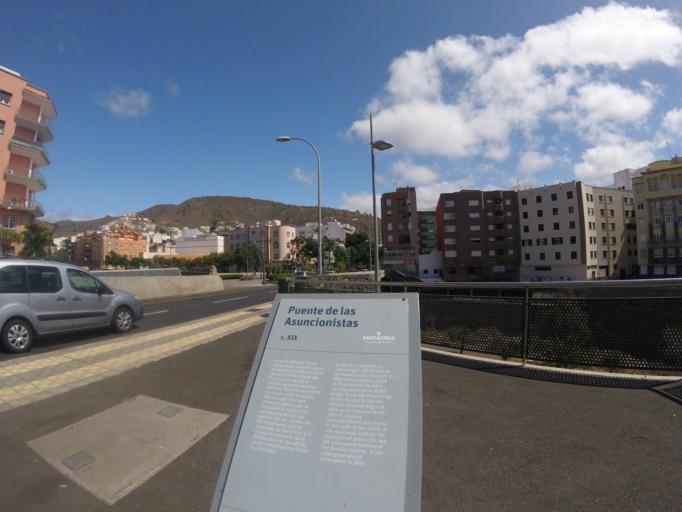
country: ES
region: Canary Islands
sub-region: Provincia de Santa Cruz de Tenerife
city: Santa Cruz de Tenerife
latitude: 28.4656
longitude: -16.2620
